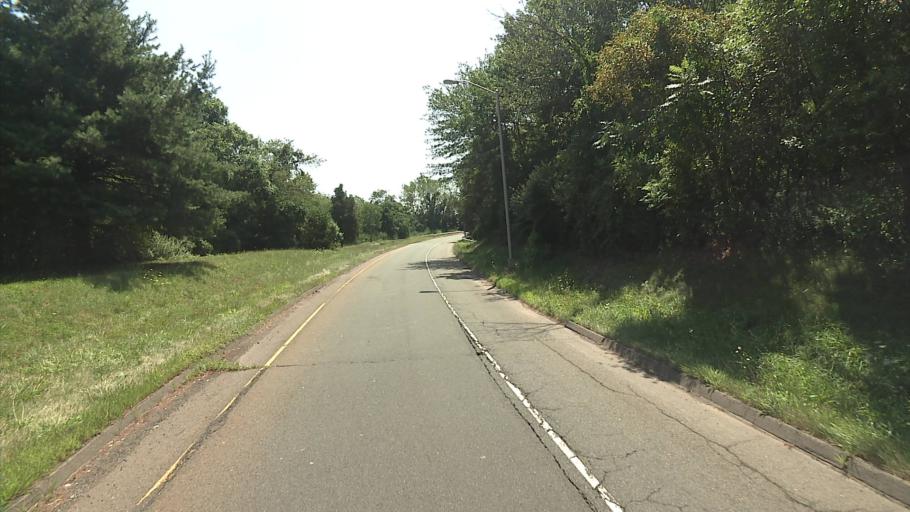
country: US
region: Connecticut
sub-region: New Haven County
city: Branford
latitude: 41.2843
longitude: -72.8368
